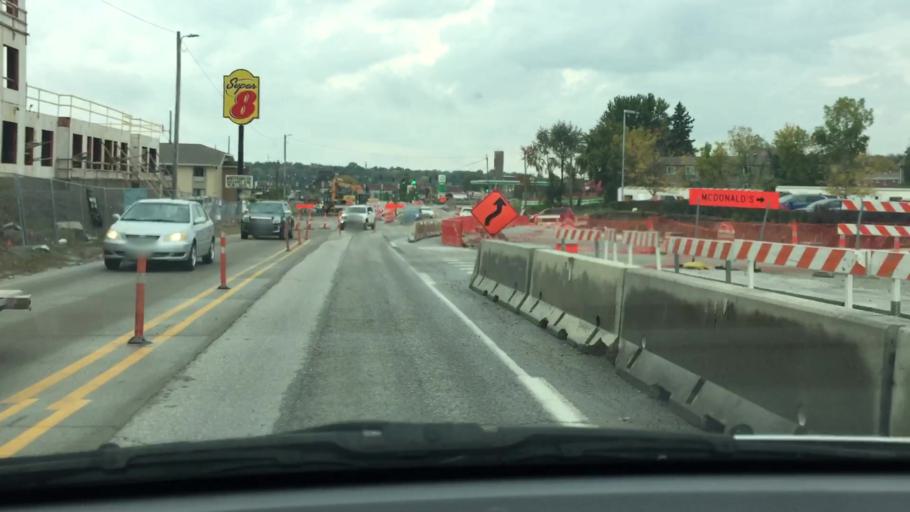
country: US
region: Iowa
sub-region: Johnson County
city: Coralville
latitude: 41.6784
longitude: -91.5659
